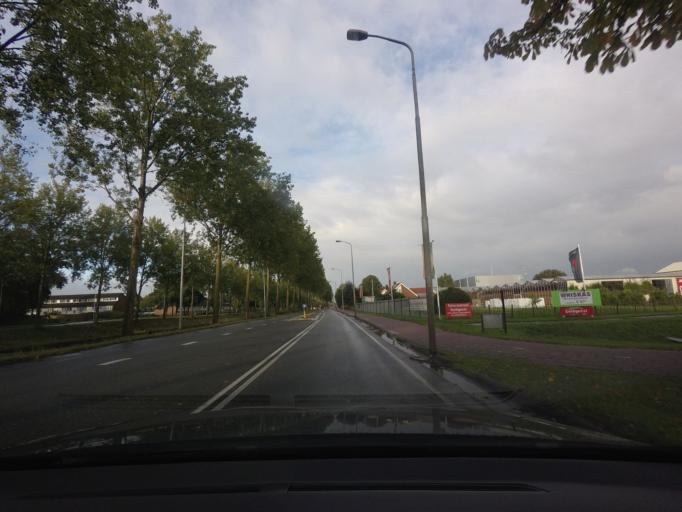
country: NL
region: South Holland
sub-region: Gemeente Kaag en Braassem
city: Oude Wetering
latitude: 52.2576
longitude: 4.6246
